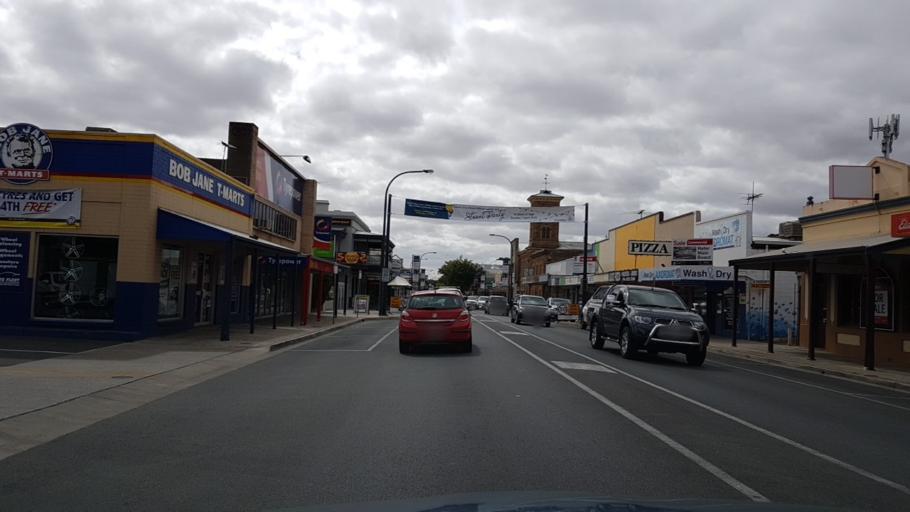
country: AU
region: South Australia
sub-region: Gawler
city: Gawler
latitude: -34.6021
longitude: 138.7487
